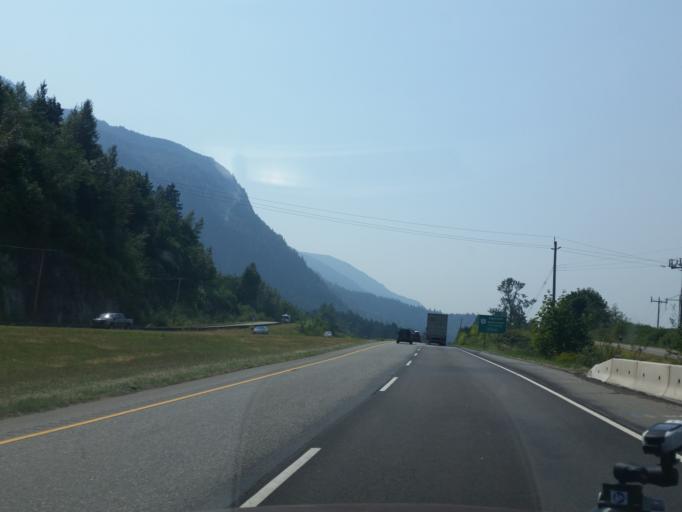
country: CA
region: British Columbia
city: Agassiz
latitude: 49.1948
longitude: -121.7353
